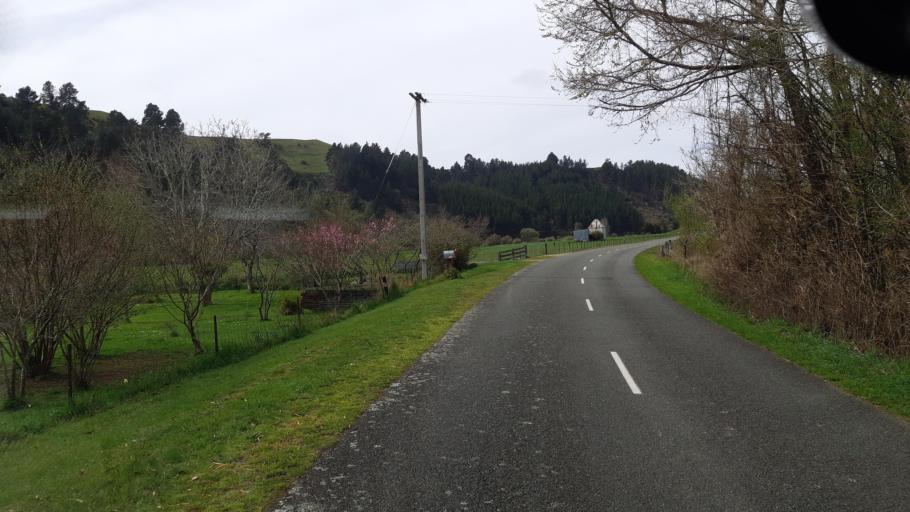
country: NZ
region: Tasman
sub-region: Tasman District
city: Wakefield
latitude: -41.3241
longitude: 172.9330
